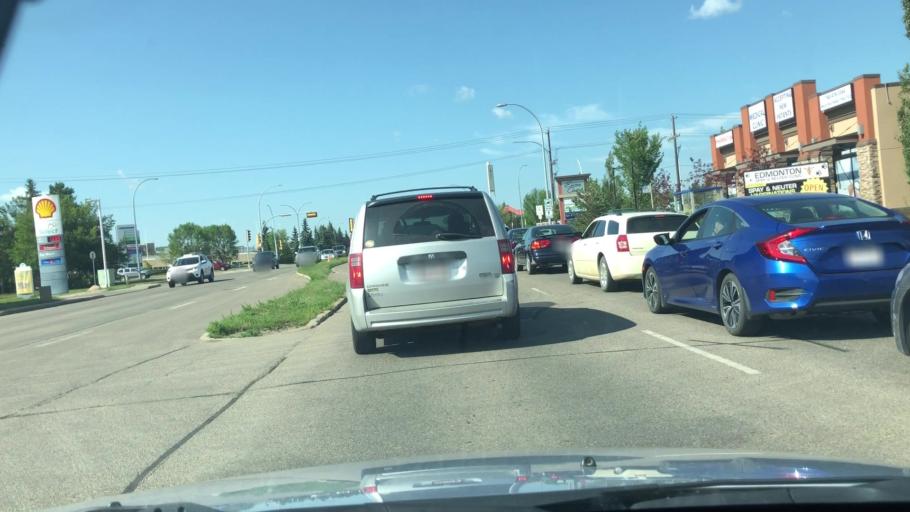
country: CA
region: Alberta
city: Edmonton
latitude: 53.5983
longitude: -113.4429
